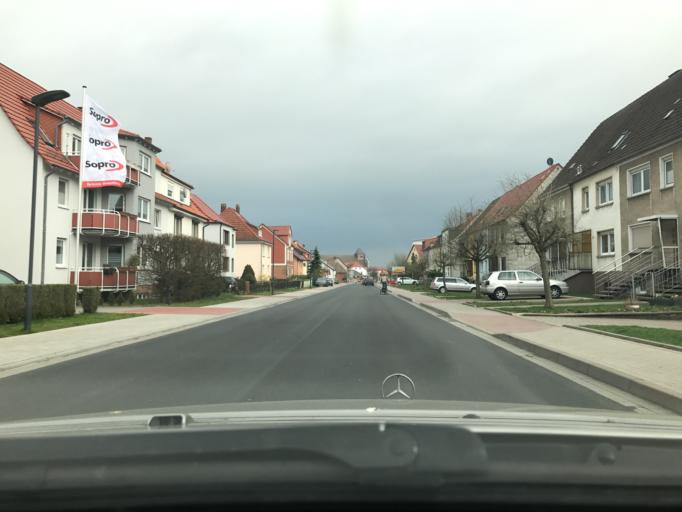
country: DE
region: Thuringia
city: Dingelstadt
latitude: 51.3180
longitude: 10.3099
